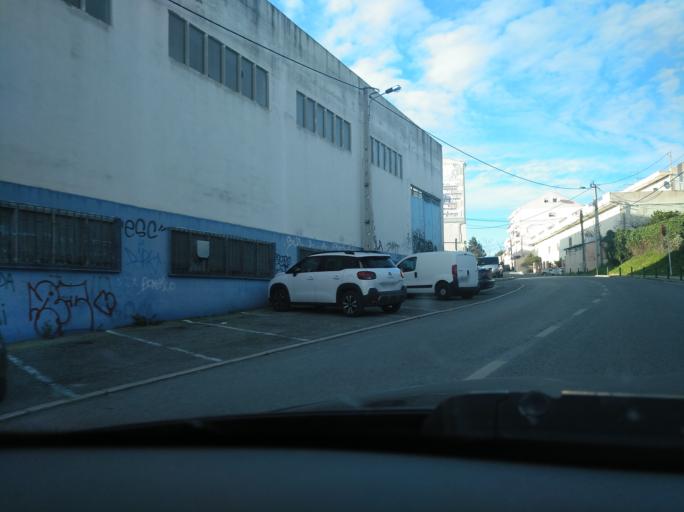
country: PT
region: Lisbon
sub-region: Loures
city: Unhos
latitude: 38.8179
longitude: -9.1185
